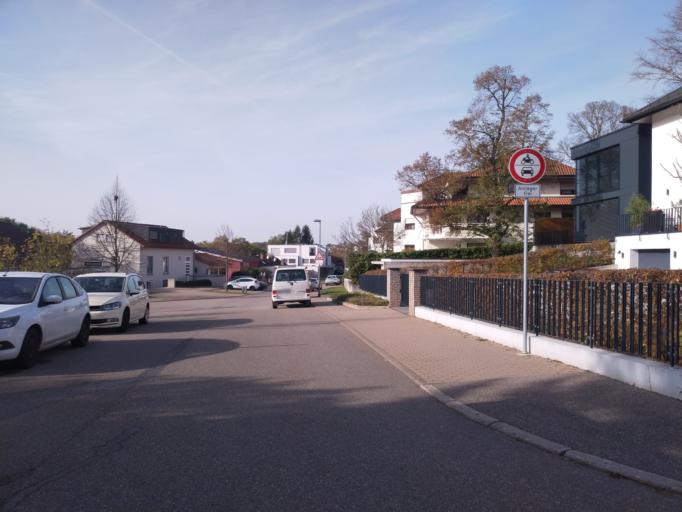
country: DE
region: Baden-Wuerttemberg
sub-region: Karlsruhe Region
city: Pforzheim
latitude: 48.8766
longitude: 8.6867
